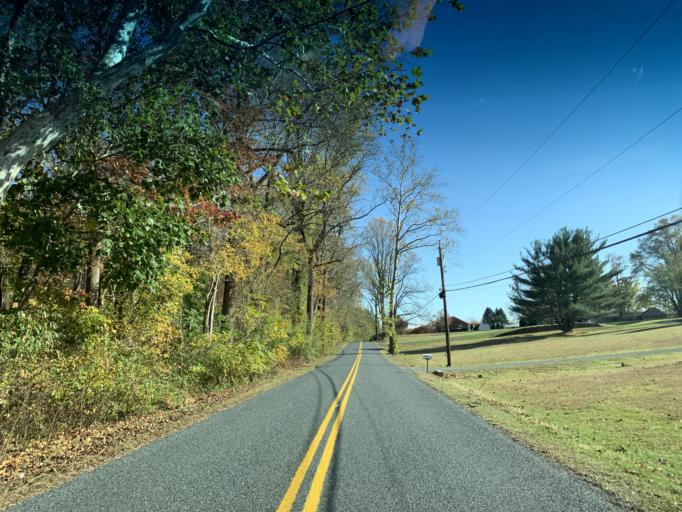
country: US
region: Maryland
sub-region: Harford County
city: Joppatowne
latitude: 39.4776
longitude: -76.3427
